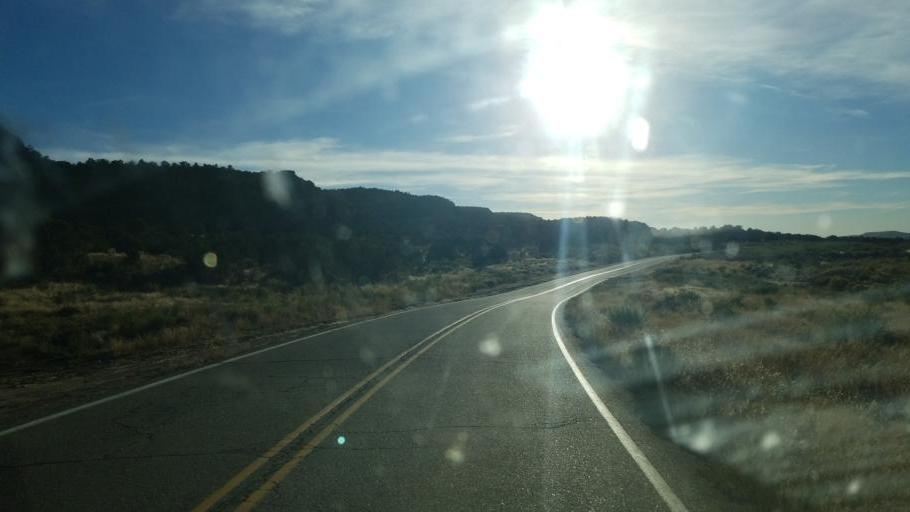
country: US
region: New Mexico
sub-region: San Juan County
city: Bloomfield
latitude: 36.7372
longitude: -107.7365
